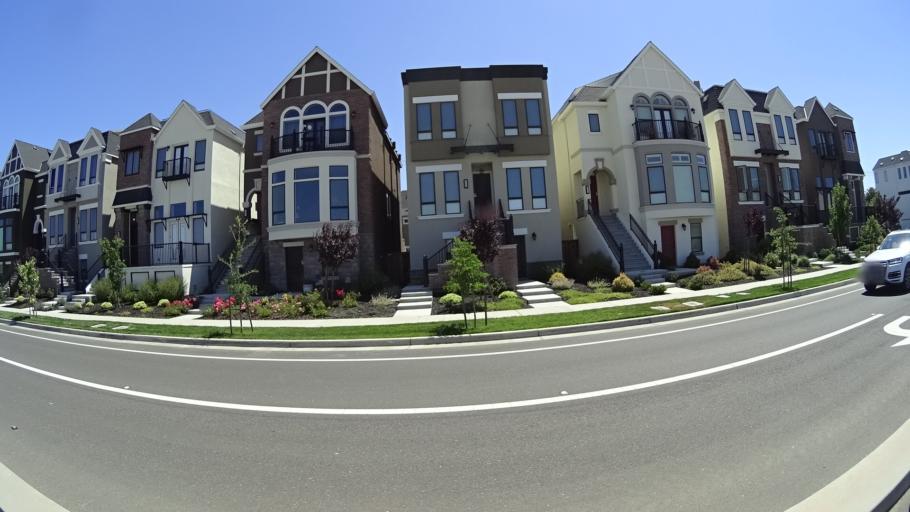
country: US
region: California
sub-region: Sacramento County
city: Sacramento
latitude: 38.5424
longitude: -121.4824
